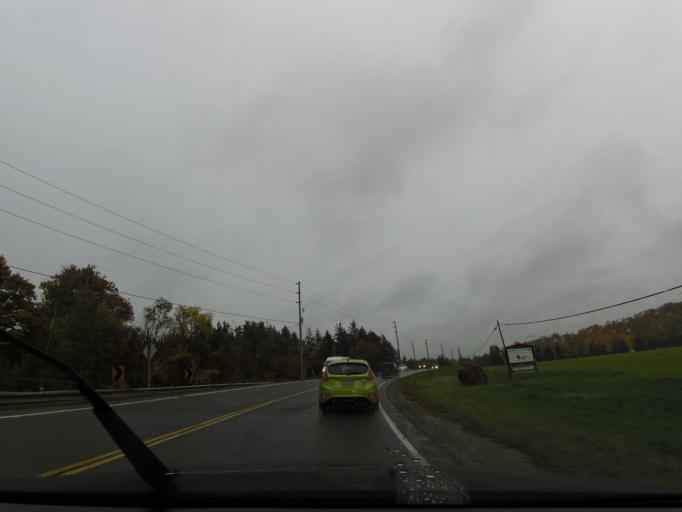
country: CA
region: Ontario
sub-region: Halton
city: Milton
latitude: 43.4556
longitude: -79.9380
